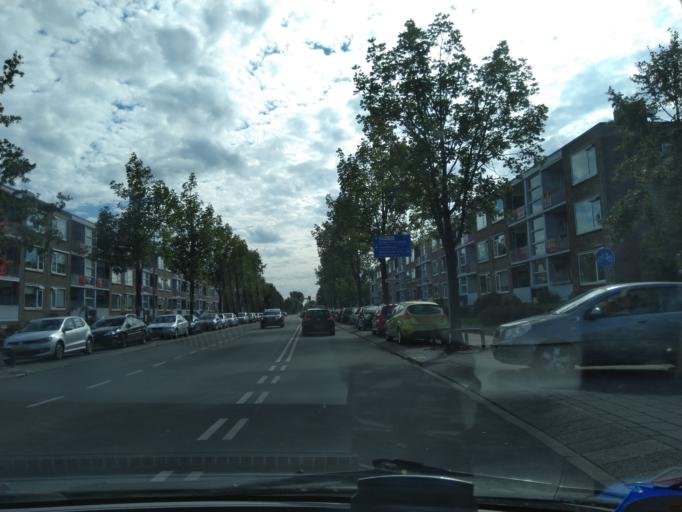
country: NL
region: Groningen
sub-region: Gemeente Groningen
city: Groningen
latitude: 53.1956
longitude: 6.5561
